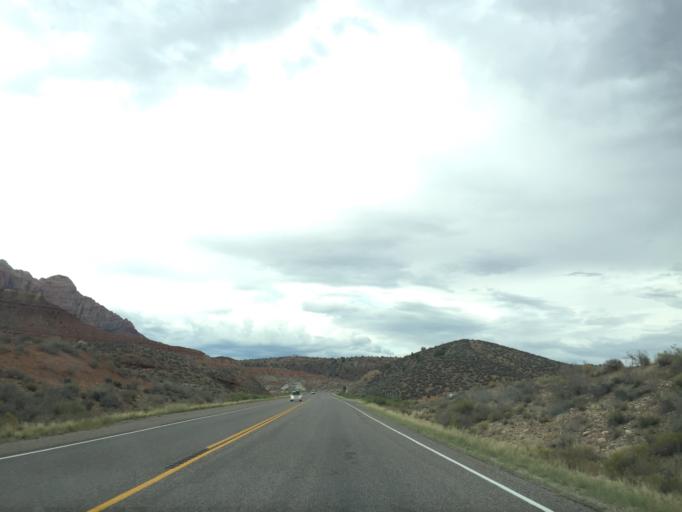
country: US
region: Utah
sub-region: Washington County
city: LaVerkin
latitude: 37.1703
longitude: -113.0763
